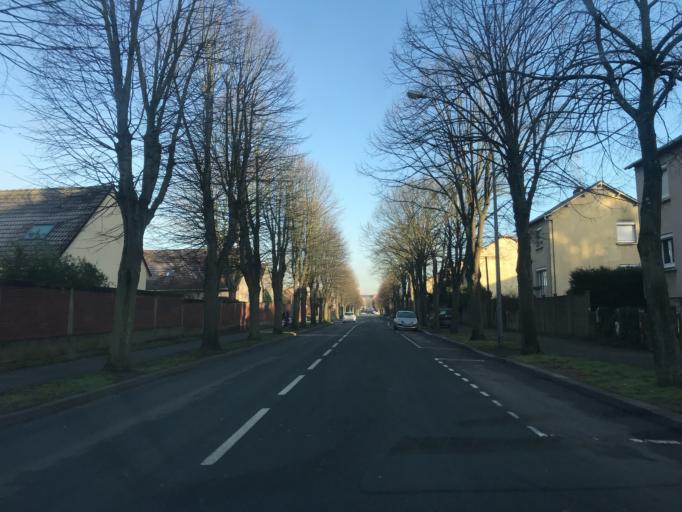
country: FR
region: Haute-Normandie
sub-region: Departement de la Seine-Maritime
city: Sotteville-les-Rouen
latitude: 49.4093
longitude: 1.1007
